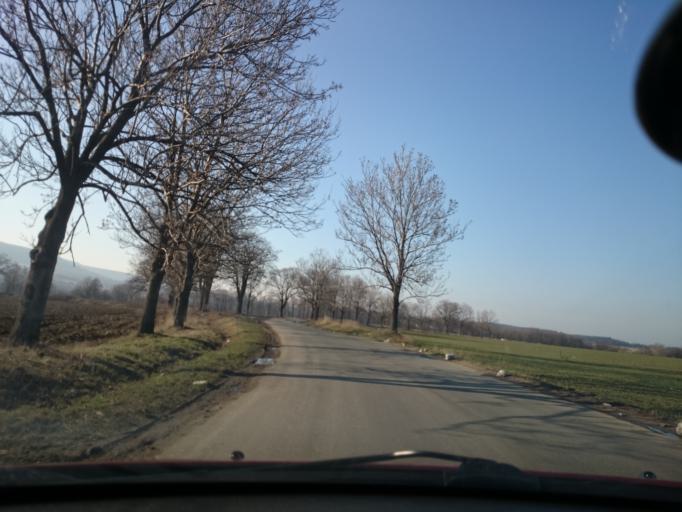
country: PL
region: Lower Silesian Voivodeship
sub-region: Powiat klodzki
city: Bystrzyca Klodzka
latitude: 50.3400
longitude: 16.5946
